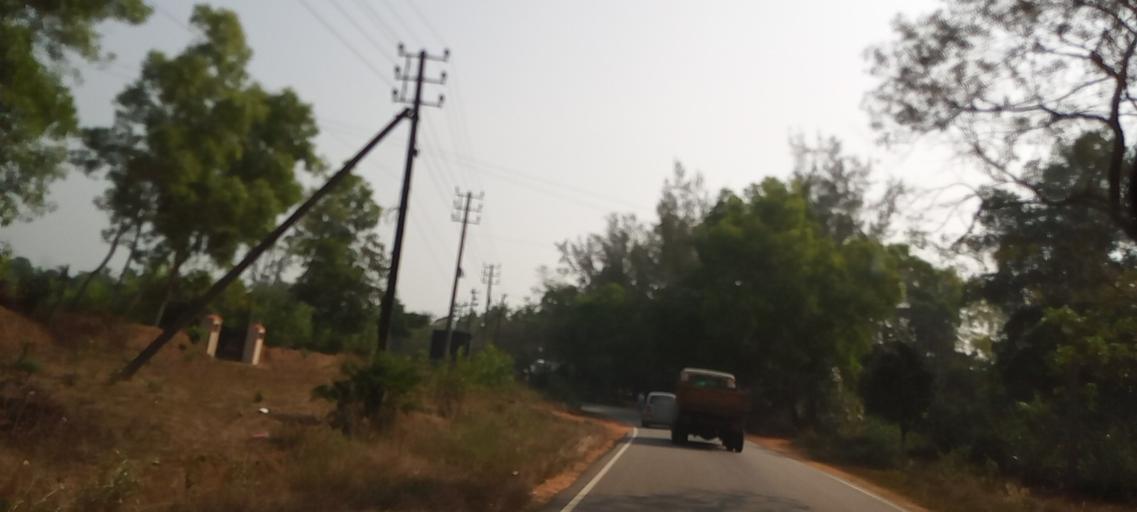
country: IN
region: Karnataka
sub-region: Udupi
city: Coondapoor
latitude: 13.5142
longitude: 74.7413
